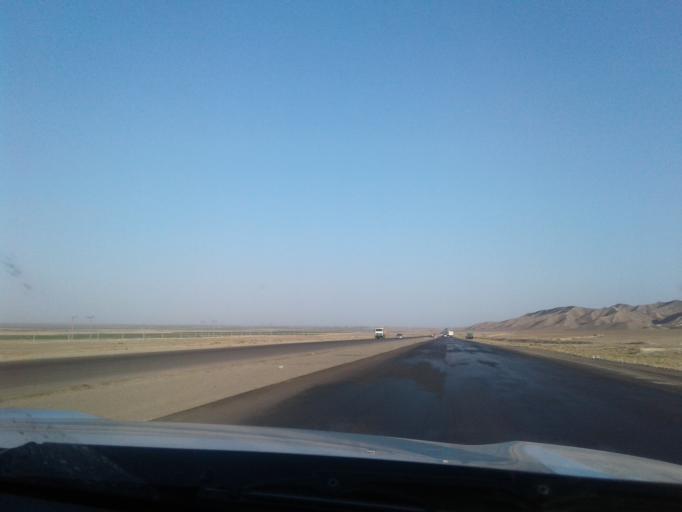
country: TM
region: Ahal
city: Baharly
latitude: 38.6171
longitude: 57.0339
